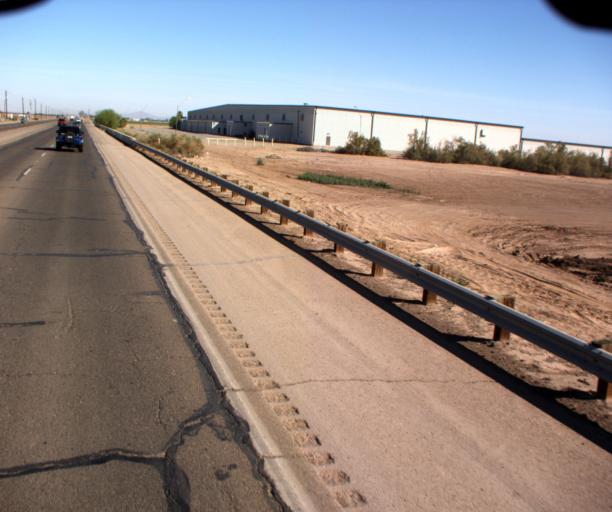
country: US
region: Arizona
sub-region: Yuma County
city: San Luis
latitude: 32.5270
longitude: -114.7866
